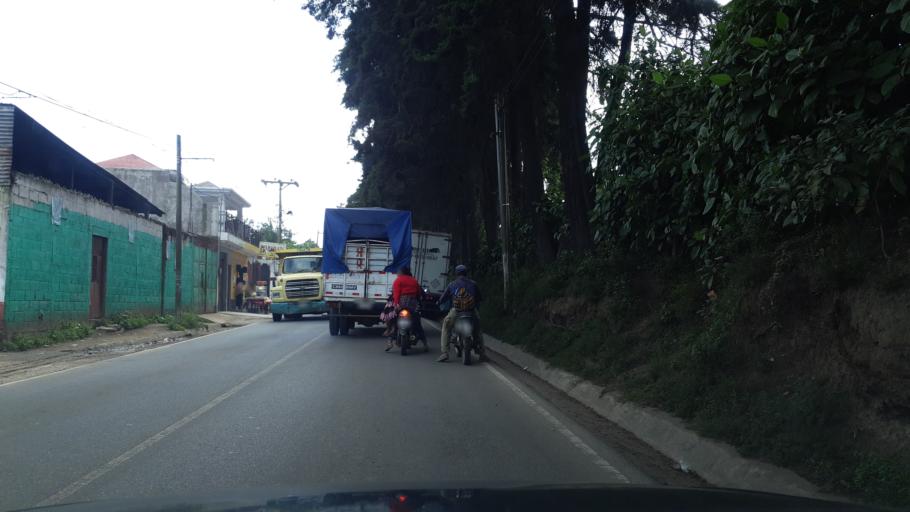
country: GT
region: Chimaltenango
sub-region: Municipio de Chimaltenango
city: Chimaltenango
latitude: 14.6658
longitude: -90.8085
